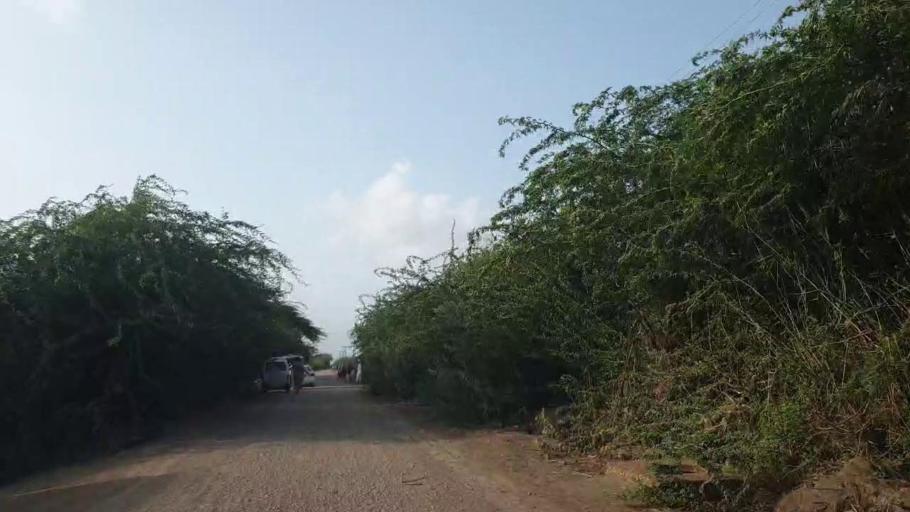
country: PK
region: Sindh
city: Kadhan
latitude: 24.6419
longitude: 69.1117
